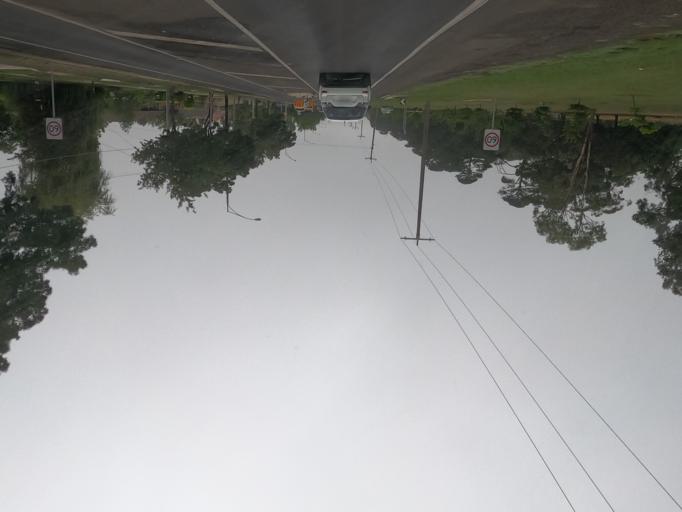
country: AU
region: Victoria
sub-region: Ballarat North
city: Newington
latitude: -37.5579
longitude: 143.8184
